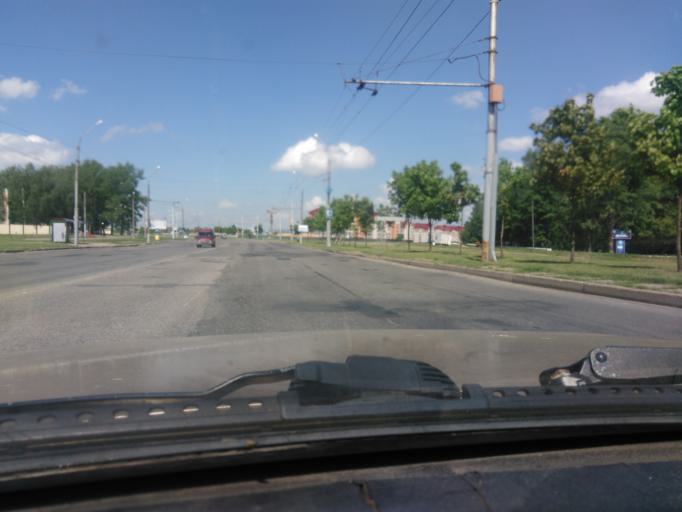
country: BY
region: Mogilev
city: Palykavichy Pyershyya
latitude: 53.9581
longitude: 30.3630
